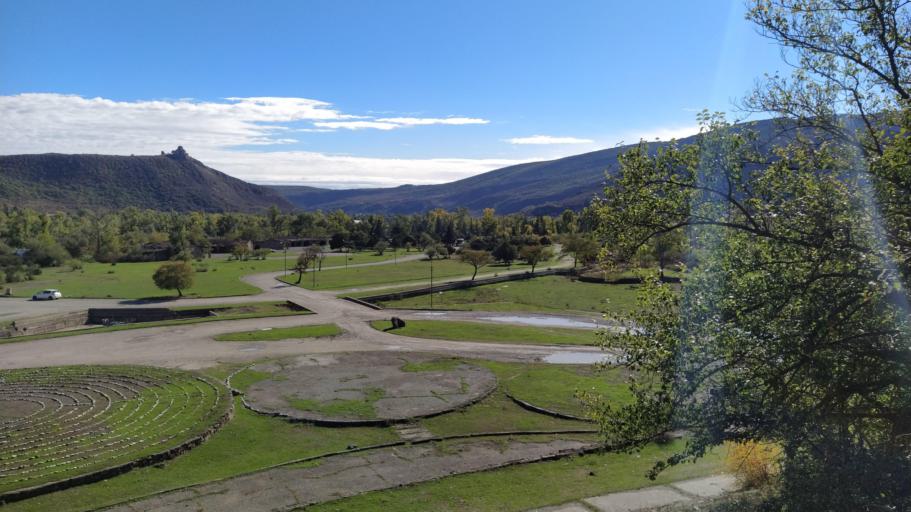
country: GE
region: Mtskheta-Mtianeti
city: Mtskheta
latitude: 41.8546
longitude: 44.7234
